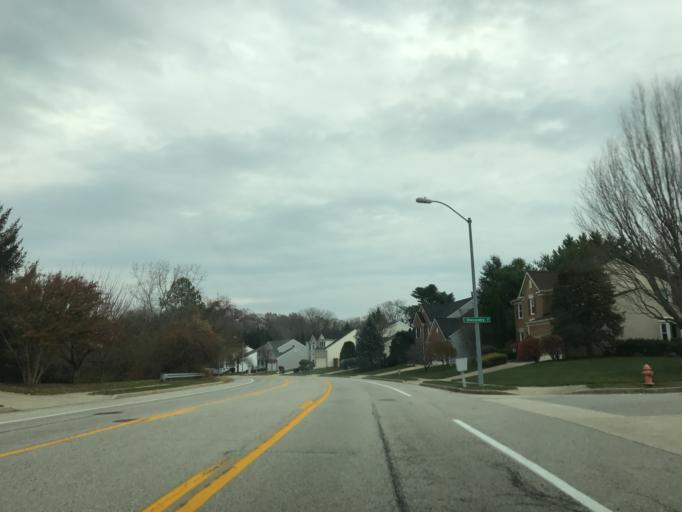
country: US
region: Maryland
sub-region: Baltimore County
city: Carney
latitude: 39.4164
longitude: -76.5275
